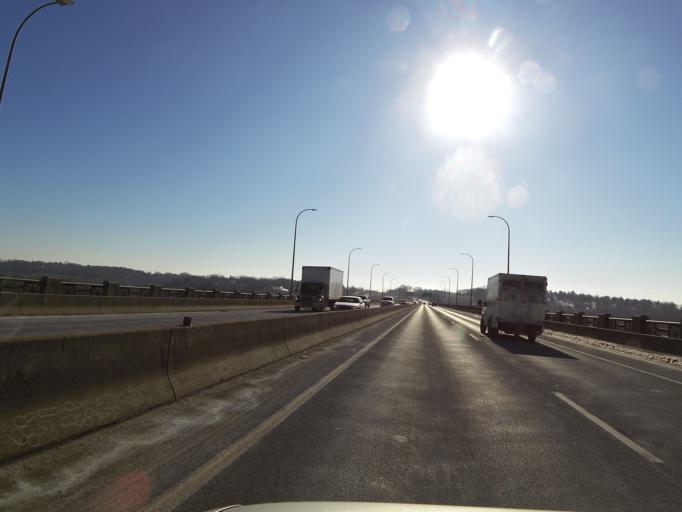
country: US
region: Minnesota
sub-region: Dakota County
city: Mendota Heights
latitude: 44.8885
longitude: -93.1795
